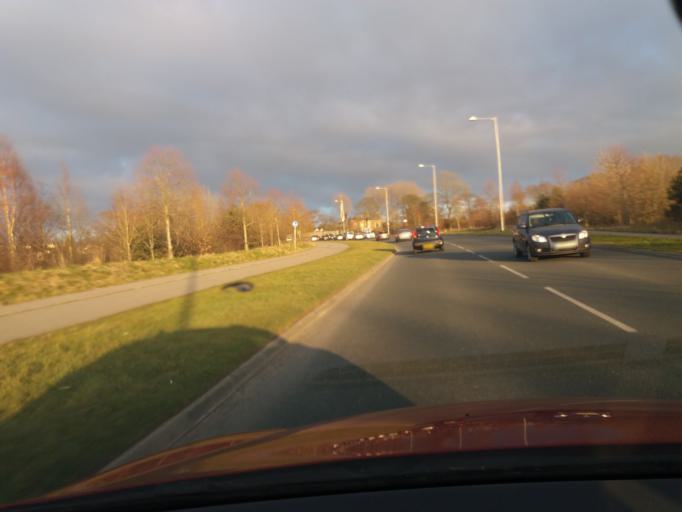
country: GB
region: England
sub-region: Lancashire
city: Chorley
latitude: 53.6731
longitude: -2.6382
